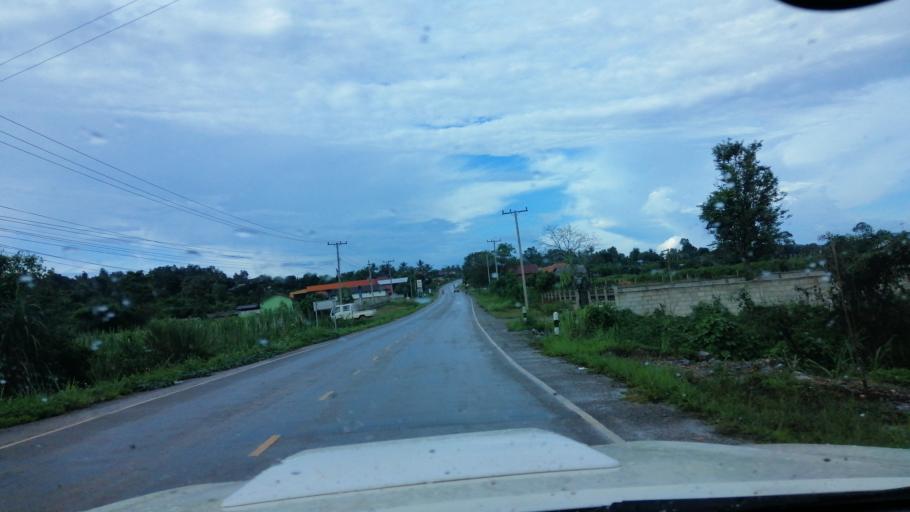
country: TH
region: Nan
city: Thung Chang
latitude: 19.6340
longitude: 100.8127
